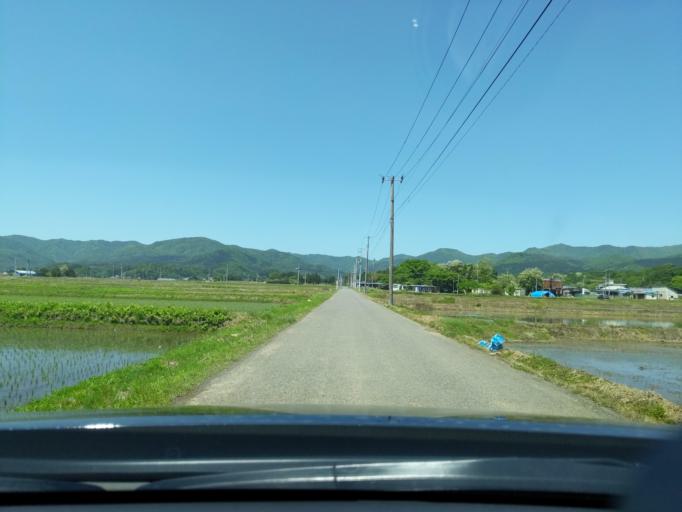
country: JP
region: Fukushima
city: Koriyama
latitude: 37.4031
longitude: 140.2748
